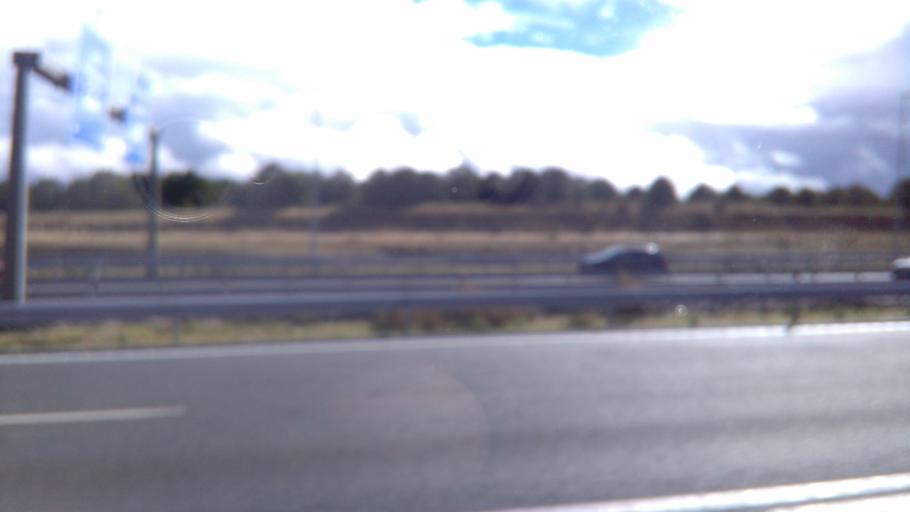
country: ES
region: Madrid
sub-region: Provincia de Madrid
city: Navalcarnero
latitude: 40.2634
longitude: -4.0418
